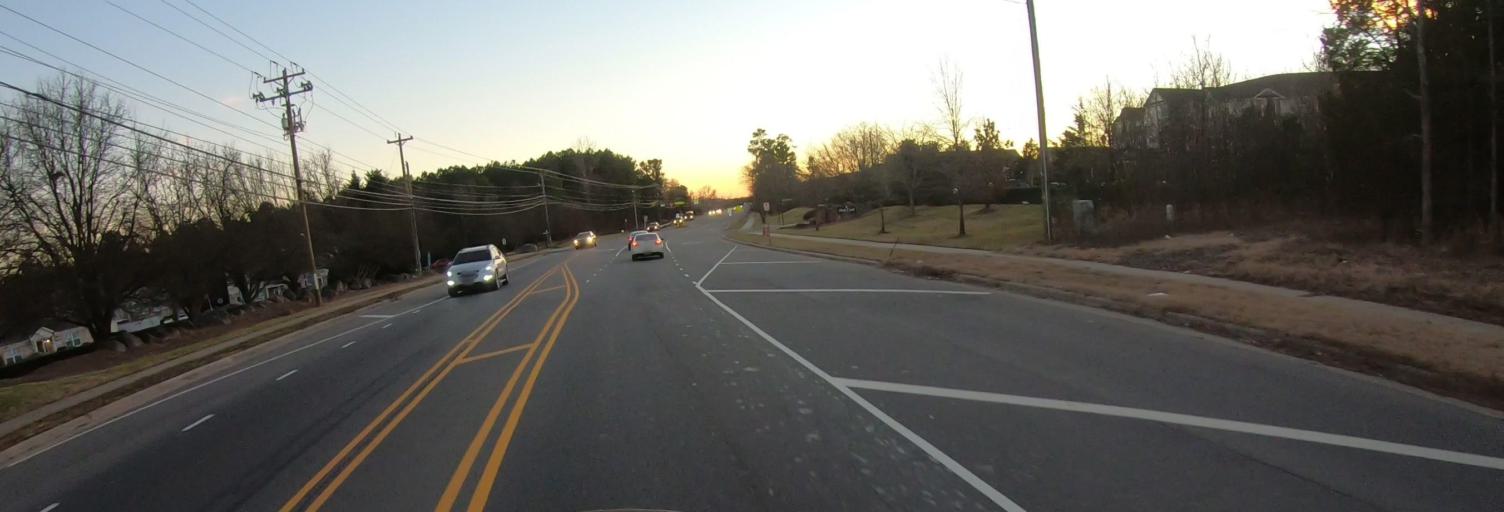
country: US
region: South Carolina
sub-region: York County
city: Lake Wylie
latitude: 35.1470
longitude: -80.9719
